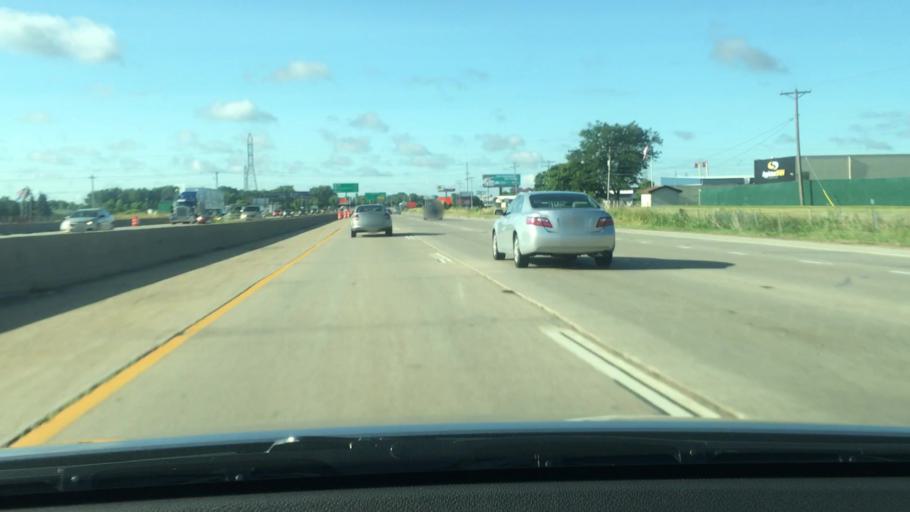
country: US
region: Wisconsin
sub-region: Winnebago County
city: Menasha
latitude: 44.2394
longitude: -88.4651
